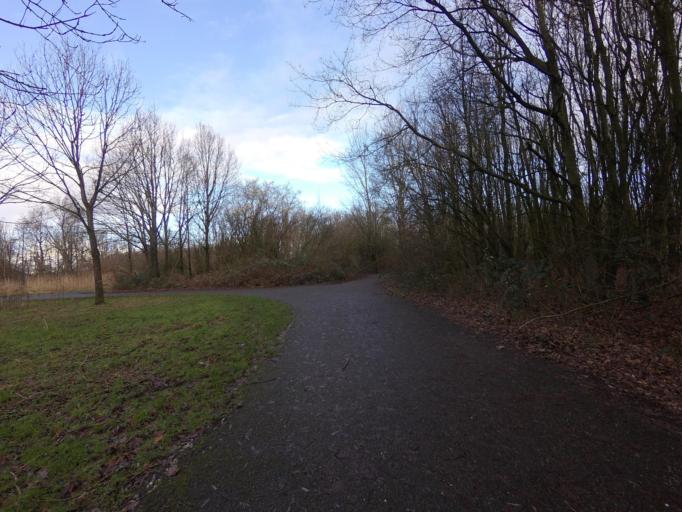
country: NL
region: Utrecht
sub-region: Gemeente Nieuwegein
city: Nieuwegein
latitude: 52.0597
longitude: 5.0727
